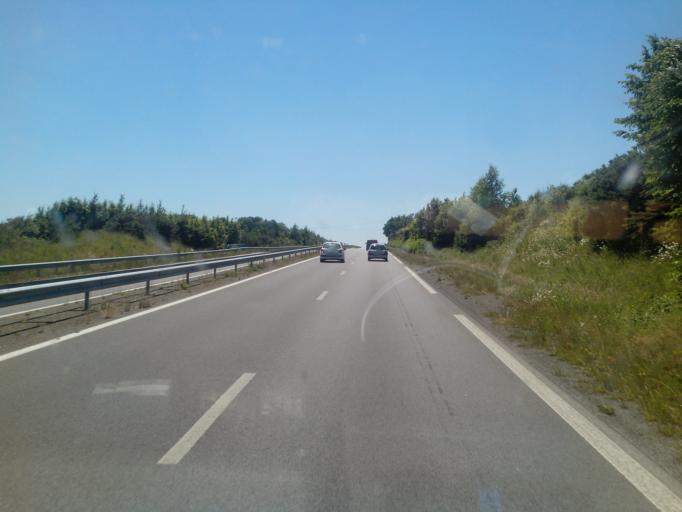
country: FR
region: Brittany
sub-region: Departement d'Ille-et-Vilaine
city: Chevaigne
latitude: 48.1952
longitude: -1.6222
